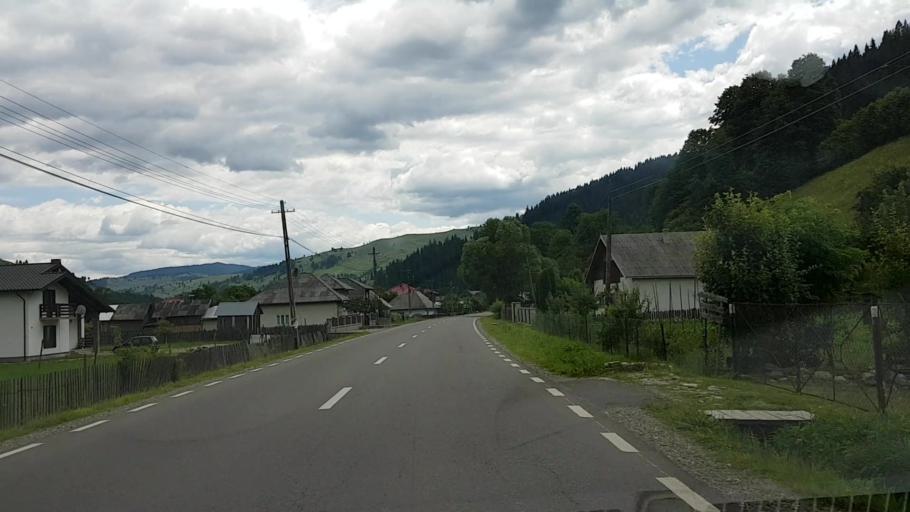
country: RO
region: Neamt
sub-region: Comuna Borca
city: Borca
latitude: 47.1892
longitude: 25.7727
